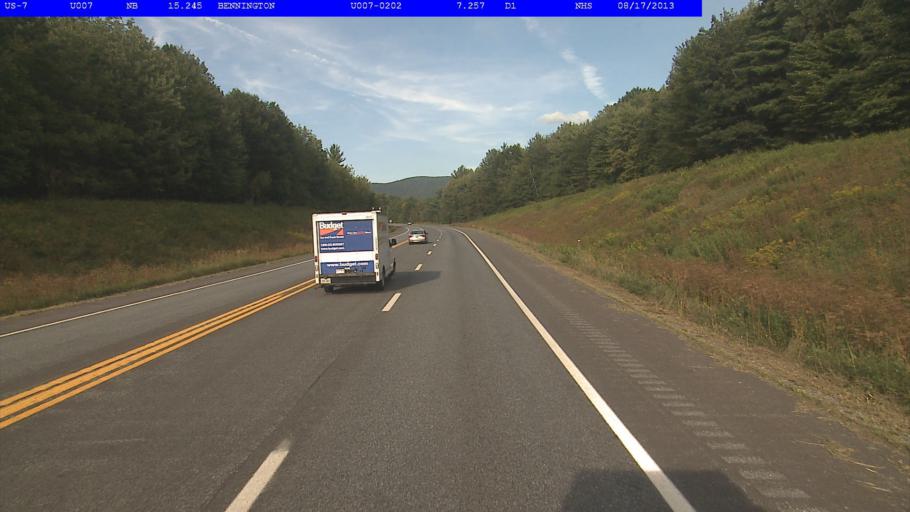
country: US
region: Vermont
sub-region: Bennington County
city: North Bennington
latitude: 42.9300
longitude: -73.1915
